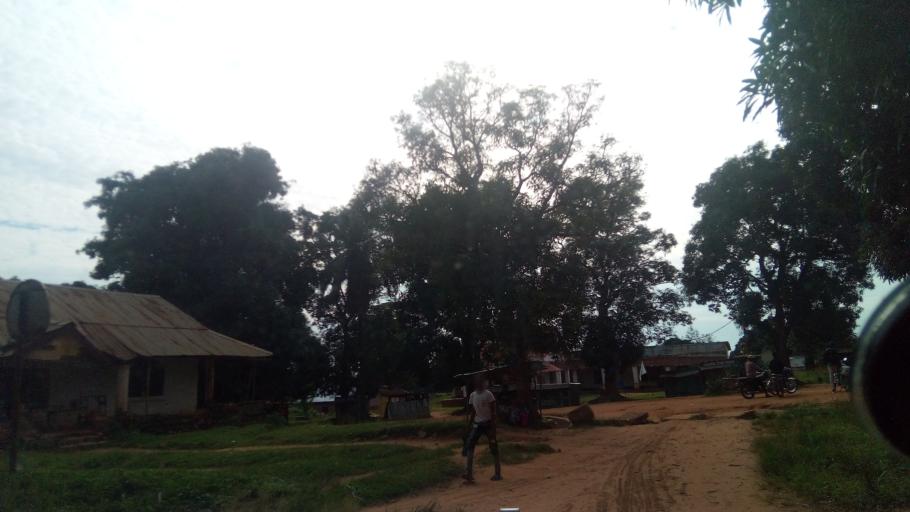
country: CD
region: Kasai-Oriental
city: Kabinda
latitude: -6.1339
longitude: 24.4864
